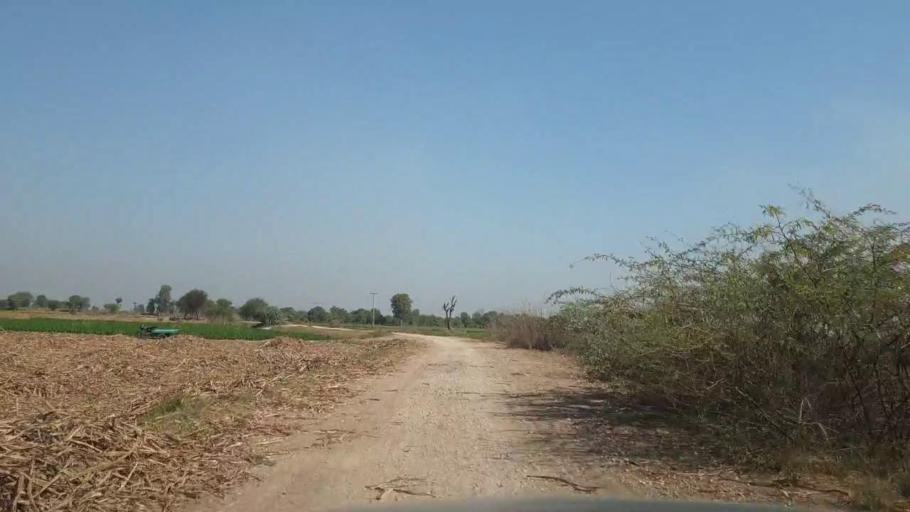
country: PK
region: Sindh
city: Tando Allahyar
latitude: 25.5879
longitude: 68.6492
